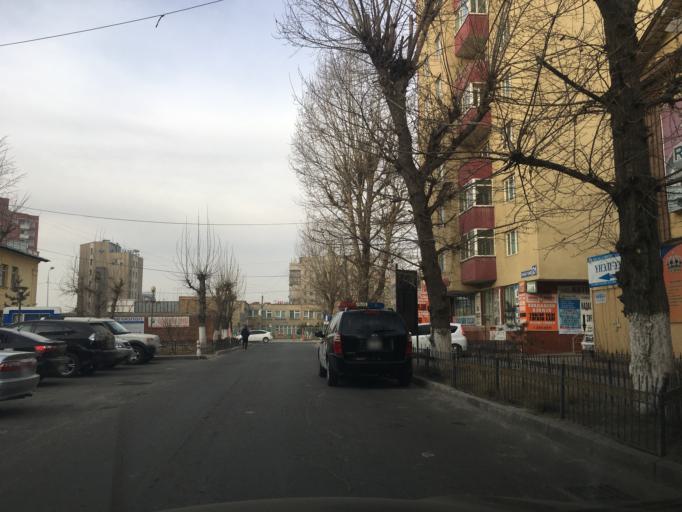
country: MN
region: Ulaanbaatar
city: Ulaanbaatar
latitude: 47.9110
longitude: 106.8784
